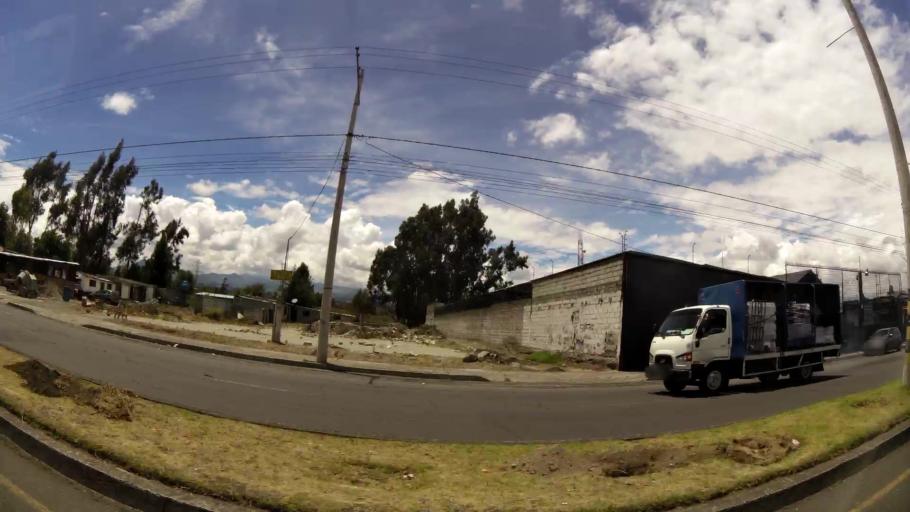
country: EC
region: Tungurahua
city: Ambato
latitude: -1.3035
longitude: -78.6008
